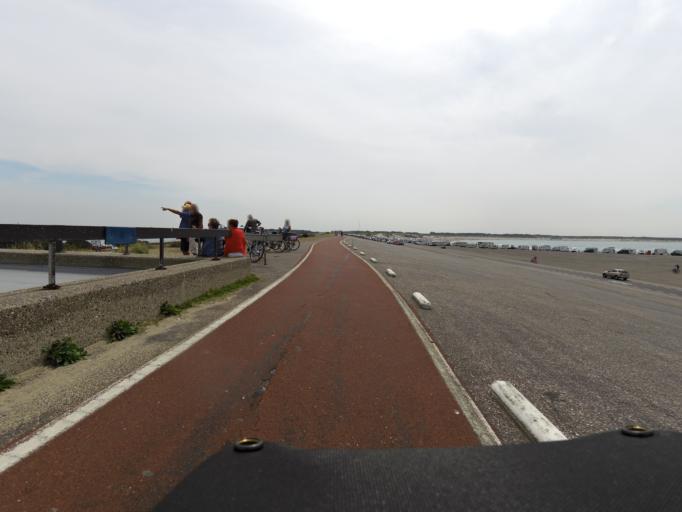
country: NL
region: Zeeland
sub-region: Schouwen-Duiveland
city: Scharendijke
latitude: 51.7485
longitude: 3.8257
